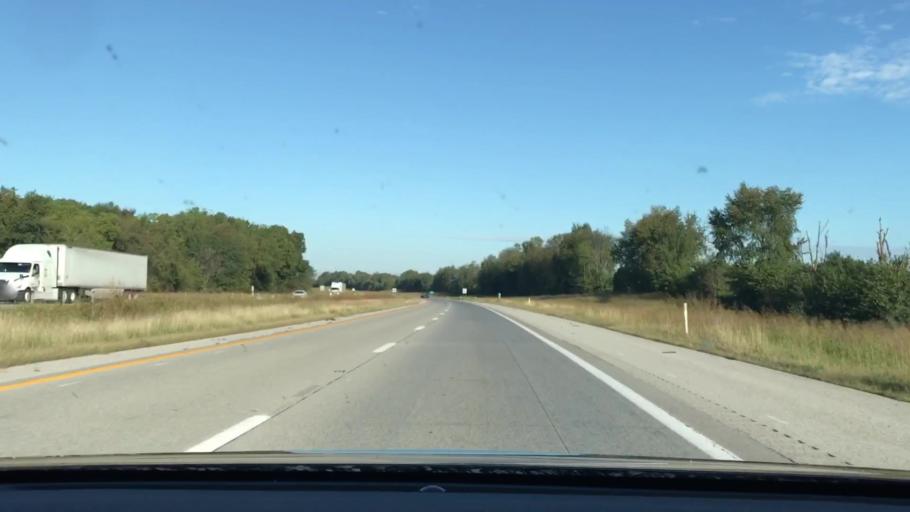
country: US
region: Kentucky
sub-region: Trigg County
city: Cadiz
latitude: 36.8397
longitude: -87.6706
